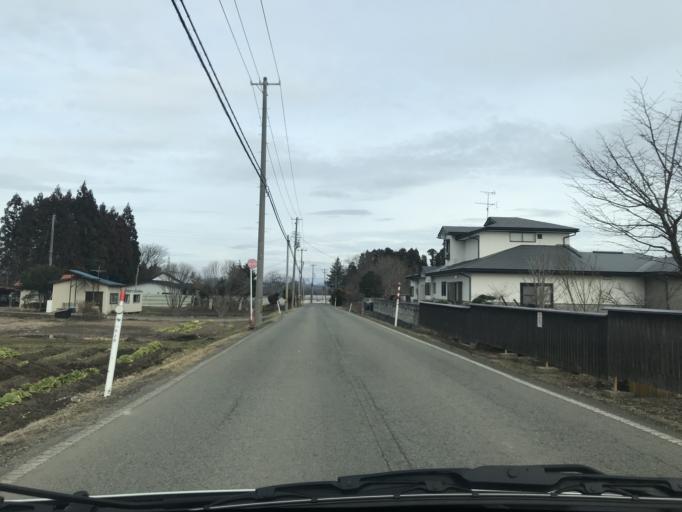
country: JP
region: Iwate
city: Kitakami
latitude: 39.2520
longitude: 141.0858
